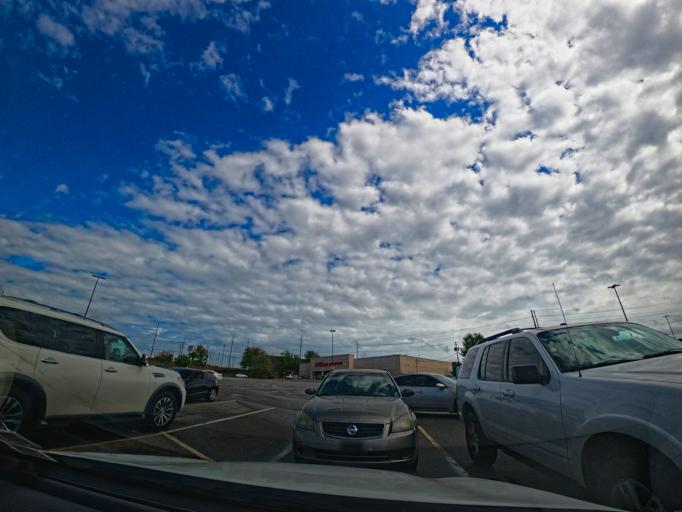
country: US
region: Alabama
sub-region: Tuscaloosa County
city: Tuscaloosa
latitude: 33.1666
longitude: -87.5189
